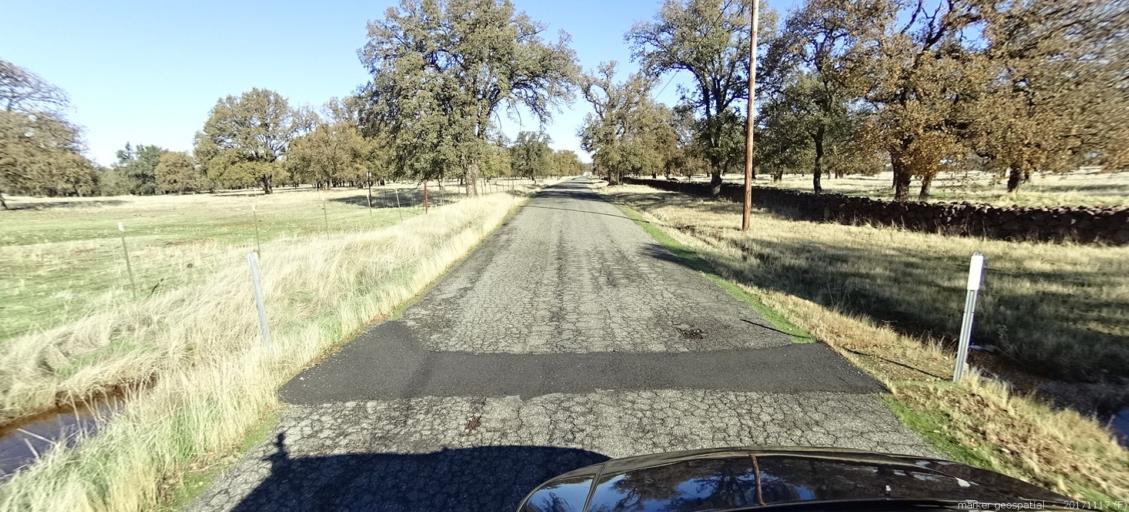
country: US
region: California
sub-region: Shasta County
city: Anderson
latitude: 40.4641
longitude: -122.1911
